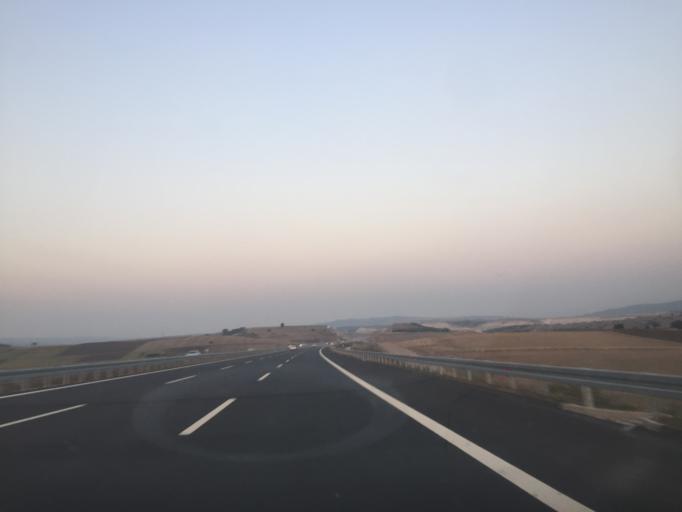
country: TR
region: Bursa
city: Mahmudiye
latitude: 40.2697
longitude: 28.6271
